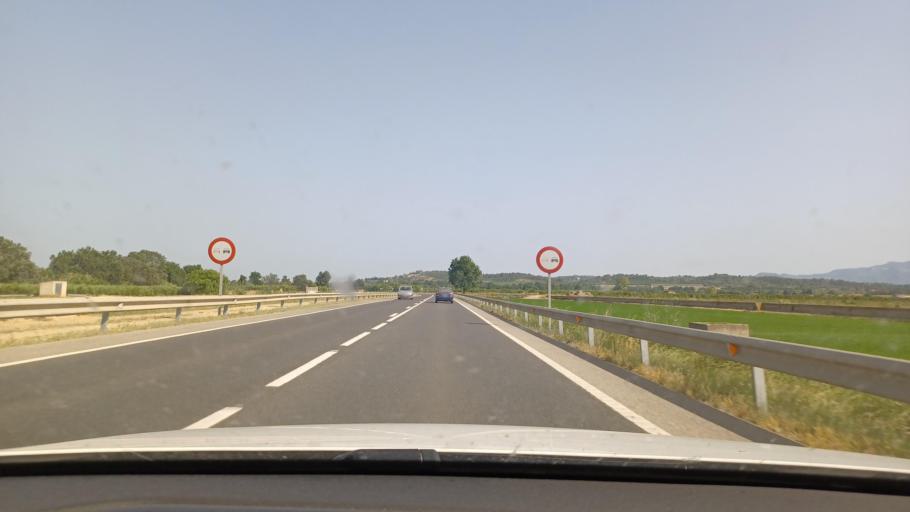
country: ES
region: Catalonia
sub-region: Provincia de Tarragona
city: Masdenverge
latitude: 40.7577
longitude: 0.5371
